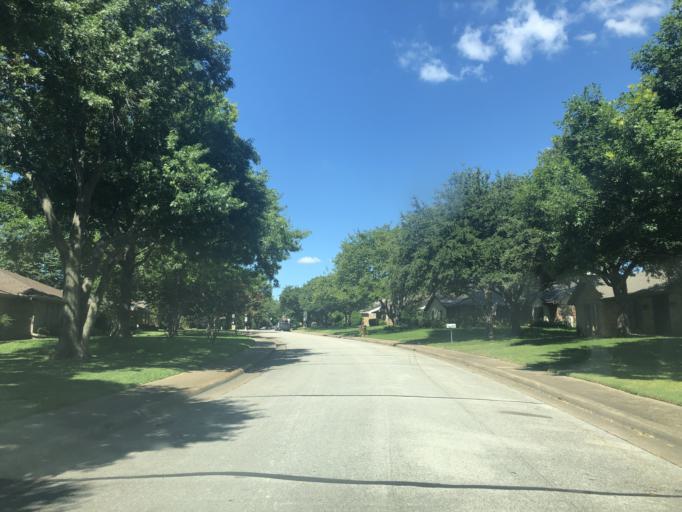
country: US
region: Texas
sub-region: Dallas County
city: Duncanville
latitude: 32.6406
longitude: -96.9285
